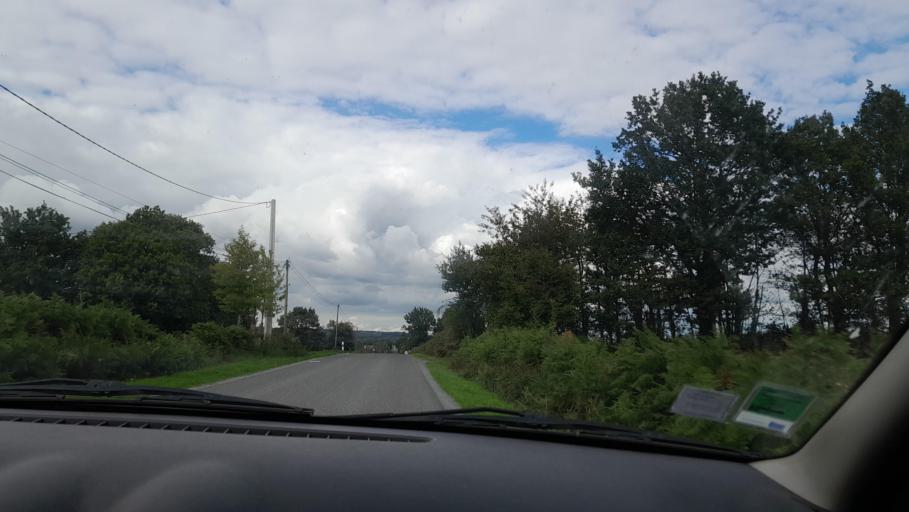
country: FR
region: Brittany
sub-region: Departement d'Ille-et-Vilaine
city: Le Pertre
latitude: 47.9748
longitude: -1.0415
